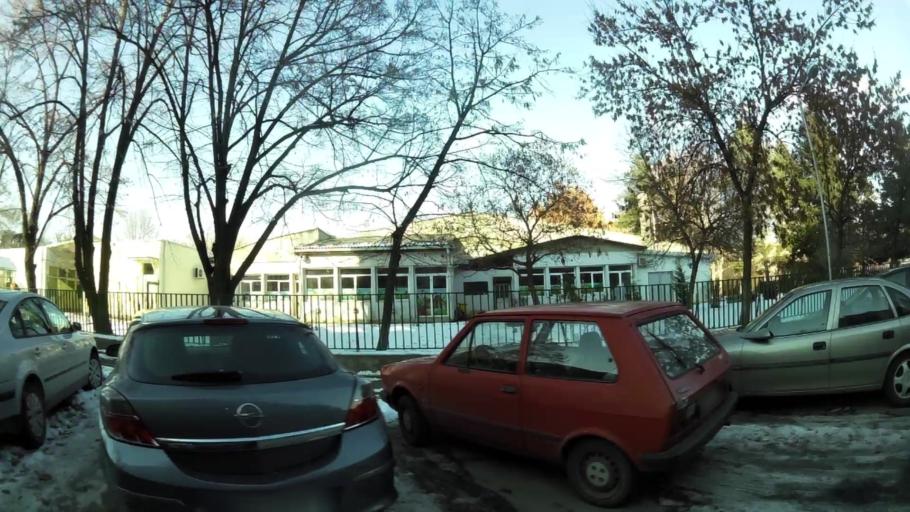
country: MK
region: Karpos
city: Skopje
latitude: 42.0043
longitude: 21.3980
